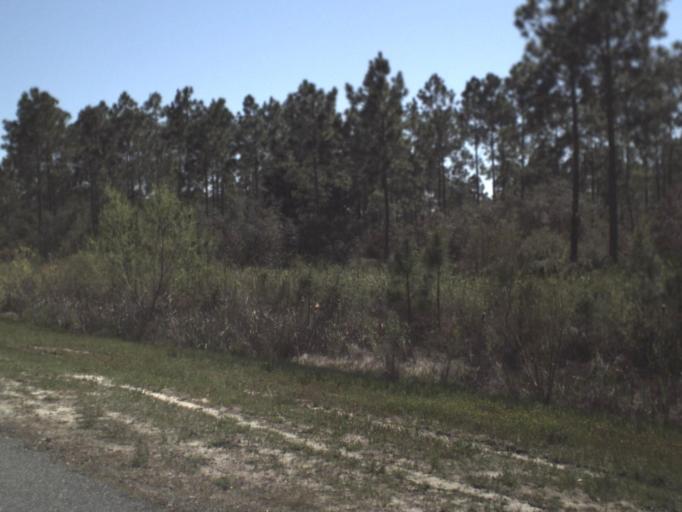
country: US
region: Florida
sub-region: Gulf County
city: Port Saint Joe
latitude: 29.8855
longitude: -85.3454
